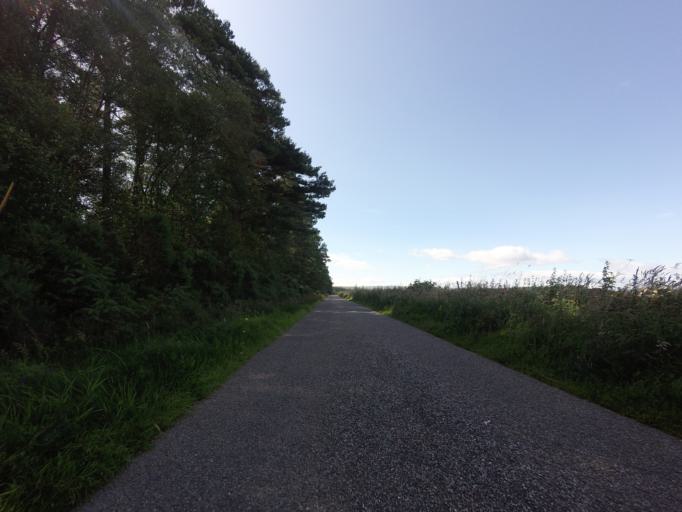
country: GB
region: Scotland
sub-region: Highland
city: Nairn
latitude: 57.5254
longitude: -3.8633
